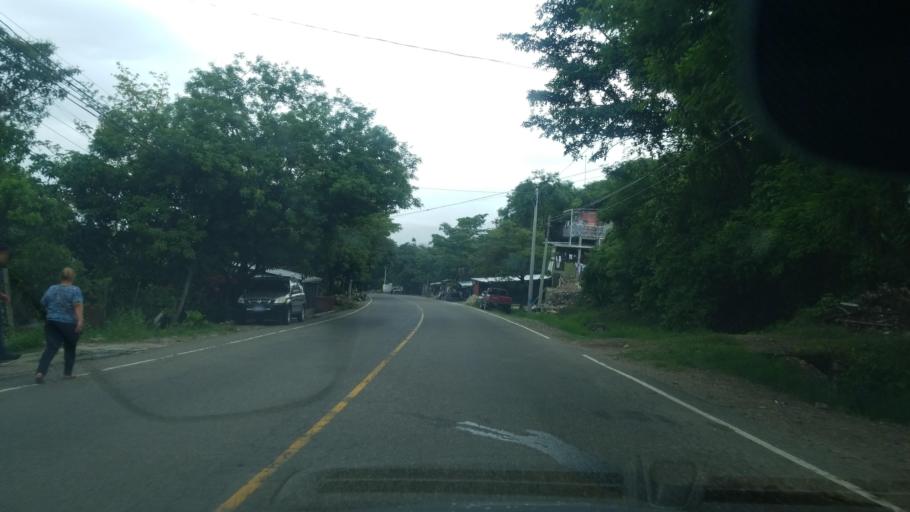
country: HN
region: Ocotepeque
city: Sinuapa
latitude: 14.4480
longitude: -89.1725
